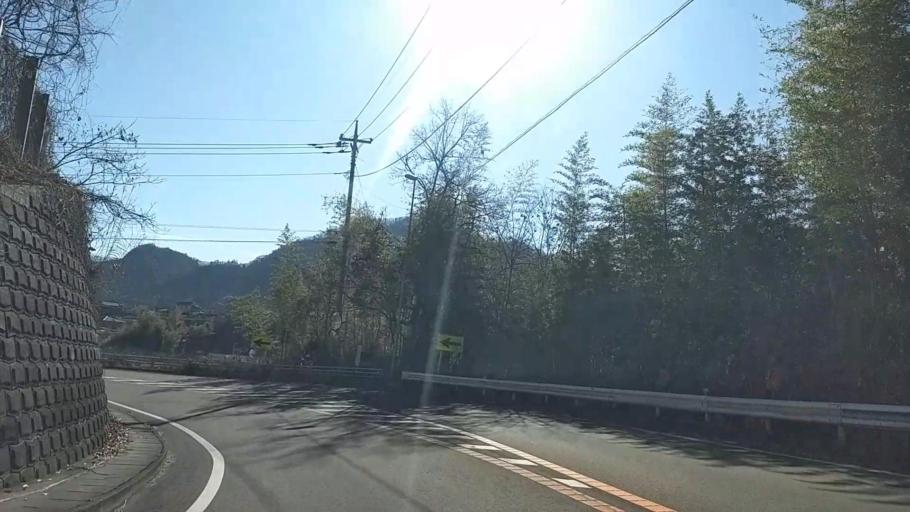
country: JP
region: Yamanashi
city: Uenohara
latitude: 35.6231
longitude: 139.1048
